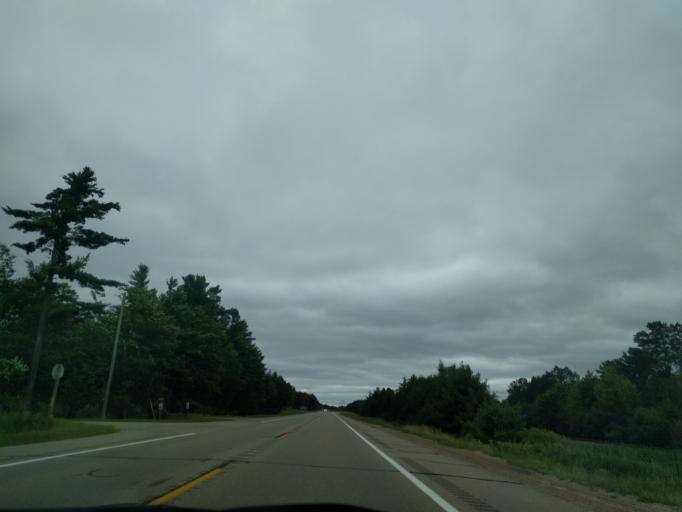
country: US
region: Michigan
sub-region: Delta County
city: Gladstone
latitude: 45.8700
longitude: -87.0635
